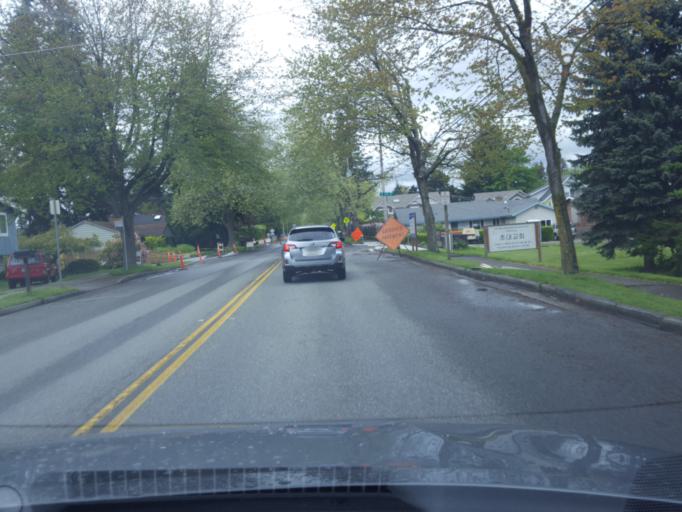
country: US
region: Washington
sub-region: King County
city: Shoreline
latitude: 47.7663
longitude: -122.3351
